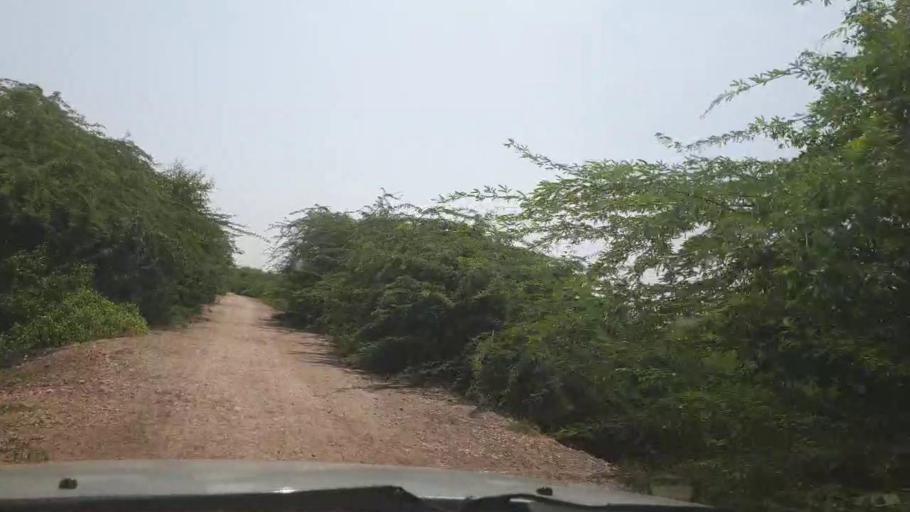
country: PK
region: Sindh
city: Tando Ghulam Ali
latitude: 25.1099
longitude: 68.8101
